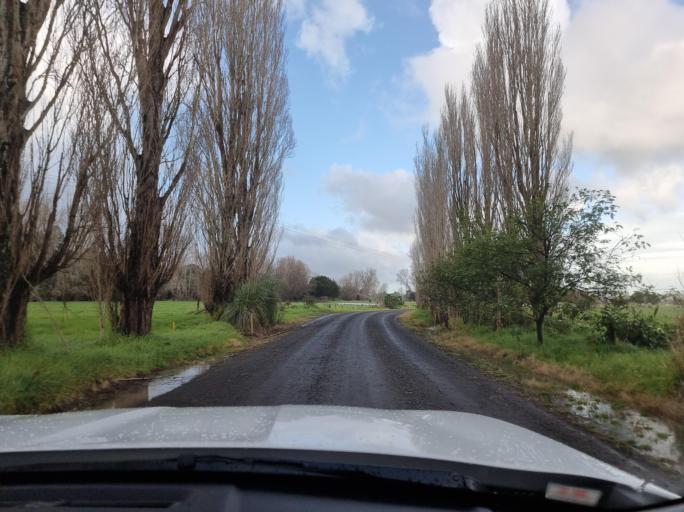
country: NZ
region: Northland
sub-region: Kaipara District
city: Dargaville
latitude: -35.7917
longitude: 173.7310
